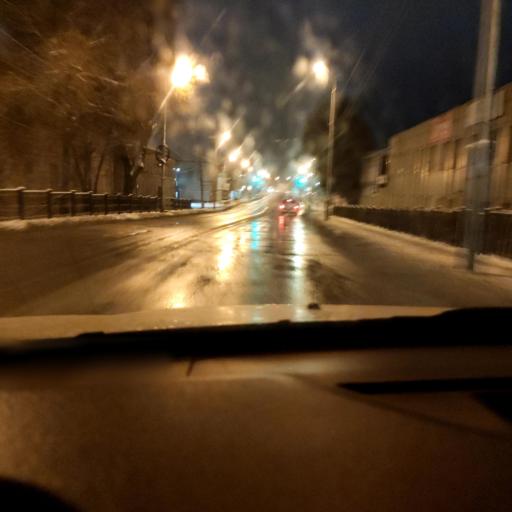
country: RU
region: Samara
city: Rozhdestveno
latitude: 53.1692
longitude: 50.0755
